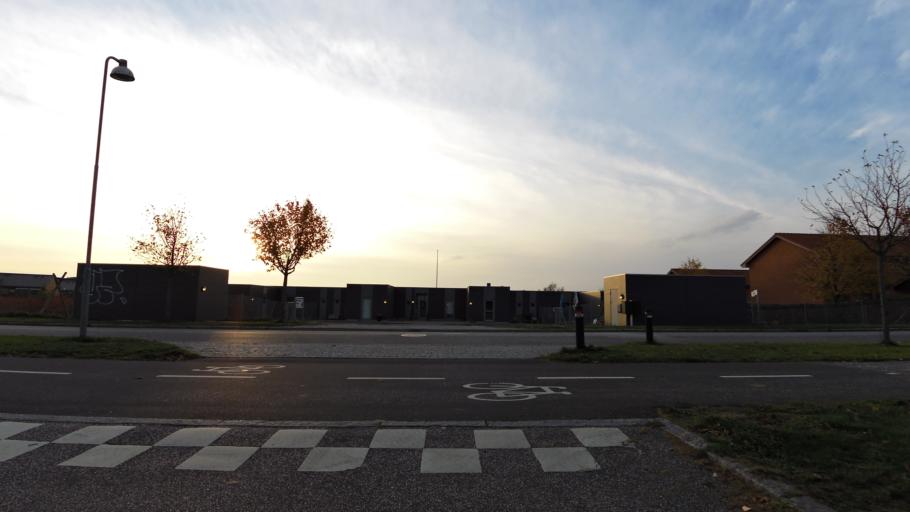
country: DK
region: Central Jutland
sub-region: Arhus Kommune
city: Stavtrup
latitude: 56.1611
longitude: 10.0947
